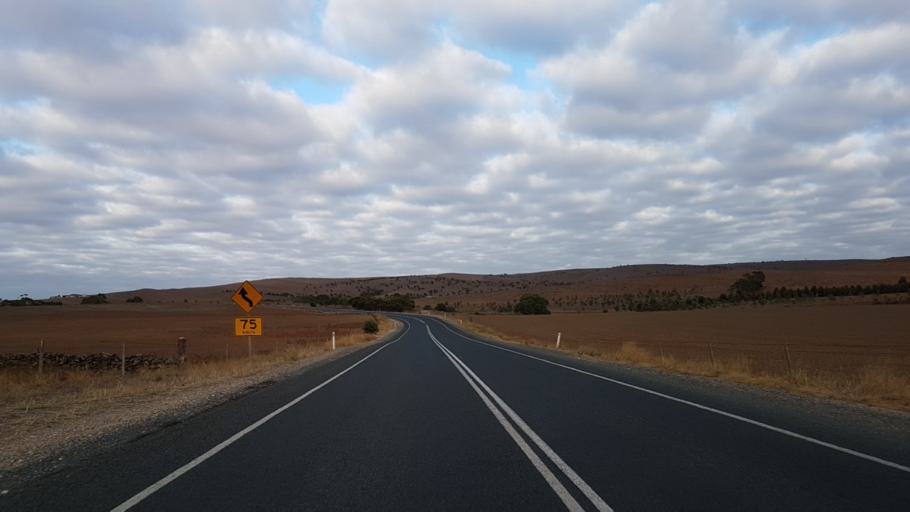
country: AU
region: South Australia
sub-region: Mount Barker
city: Callington
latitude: -35.1341
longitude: 139.0319
